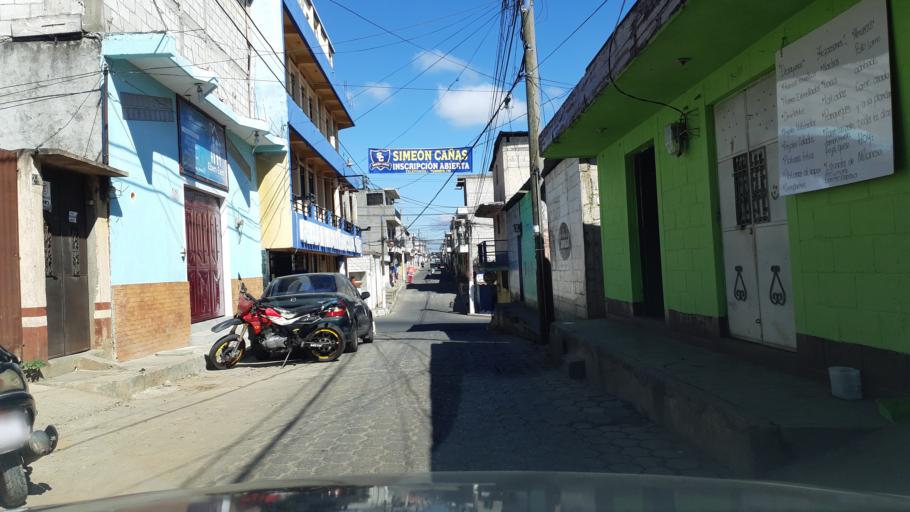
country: GT
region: Chimaltenango
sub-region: Municipio de Chimaltenango
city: Chimaltenango
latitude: 14.6625
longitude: -90.8222
